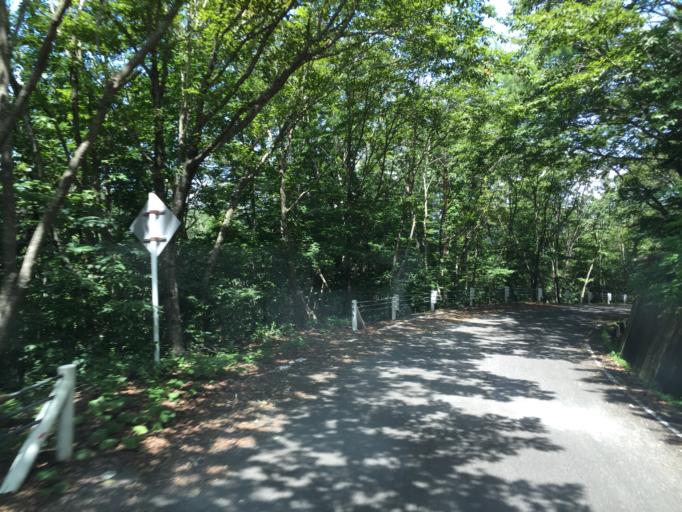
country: JP
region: Fukushima
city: Inawashiro
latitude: 37.4409
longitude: 140.0586
